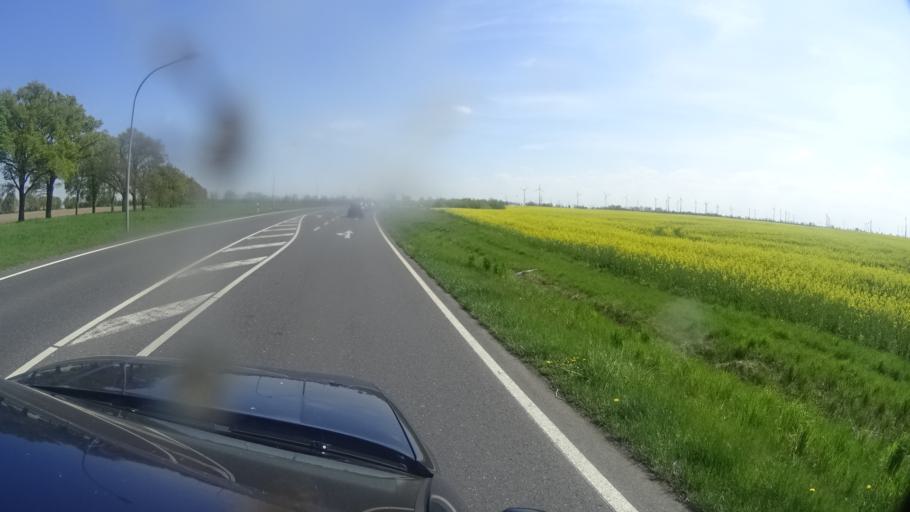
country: DE
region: Brandenburg
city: Nauen
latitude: 52.6131
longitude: 12.8390
